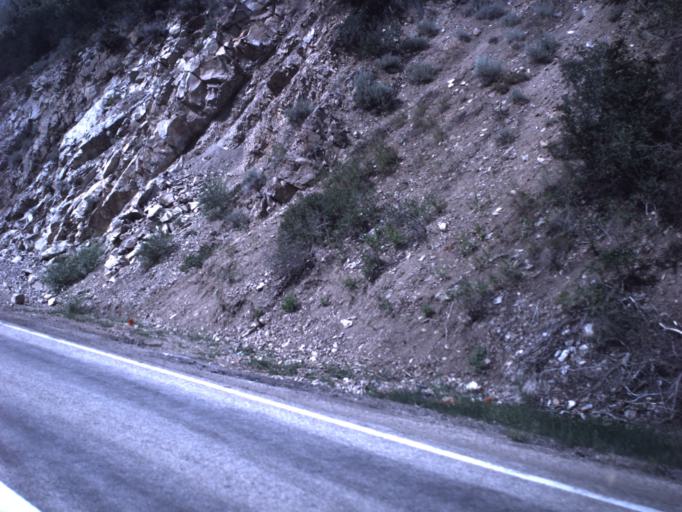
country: US
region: Utah
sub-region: Wasatch County
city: Heber
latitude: 40.3678
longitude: -111.2903
